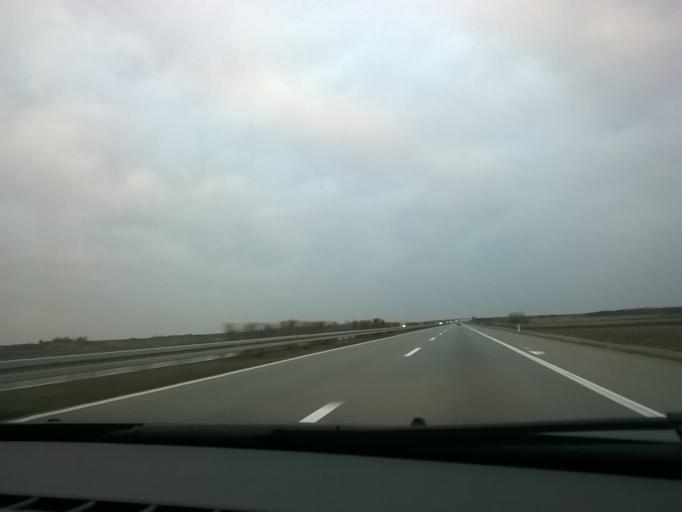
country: RS
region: Autonomna Pokrajina Vojvodina
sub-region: Juznobacki Okrug
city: Kovilj
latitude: 45.2630
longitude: 19.9791
